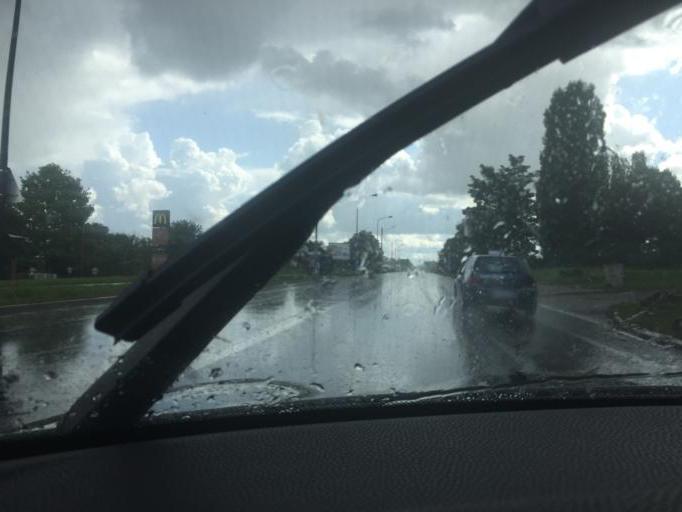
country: FR
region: Ile-de-France
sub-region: Departement du Val-de-Marne
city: Chennevieres-sur-Marne
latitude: 48.8053
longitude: 2.5343
